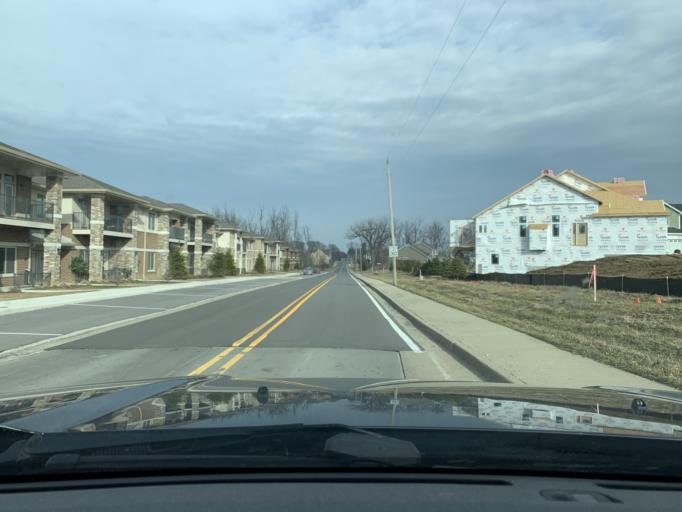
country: US
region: Indiana
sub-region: Porter County
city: Chesterton
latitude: 41.5860
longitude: -87.0408
